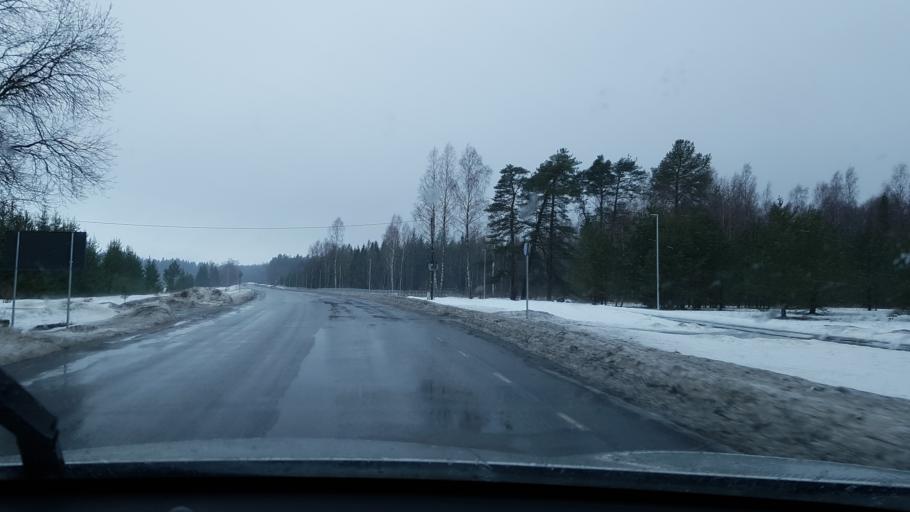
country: EE
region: Raplamaa
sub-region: Kohila vald
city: Kohila
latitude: 59.1697
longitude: 24.7270
